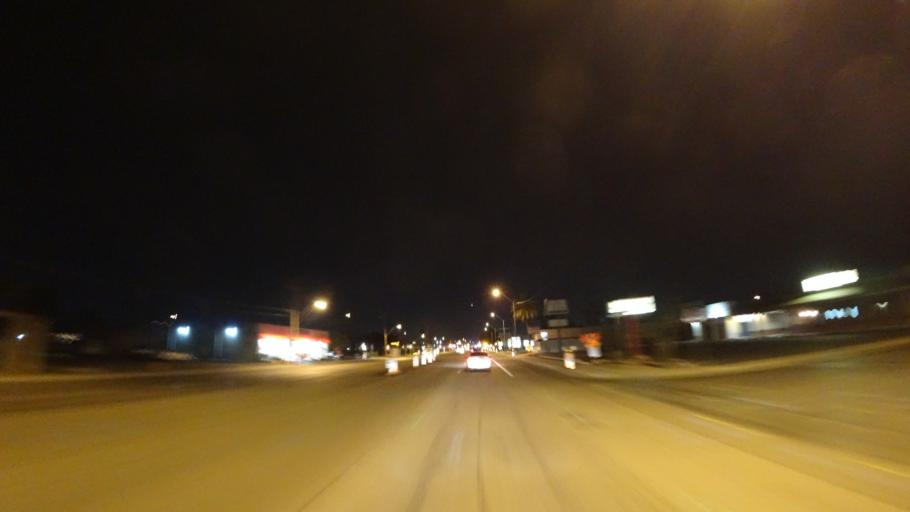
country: US
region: Arizona
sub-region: Maricopa County
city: Mesa
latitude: 33.4152
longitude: -111.8082
